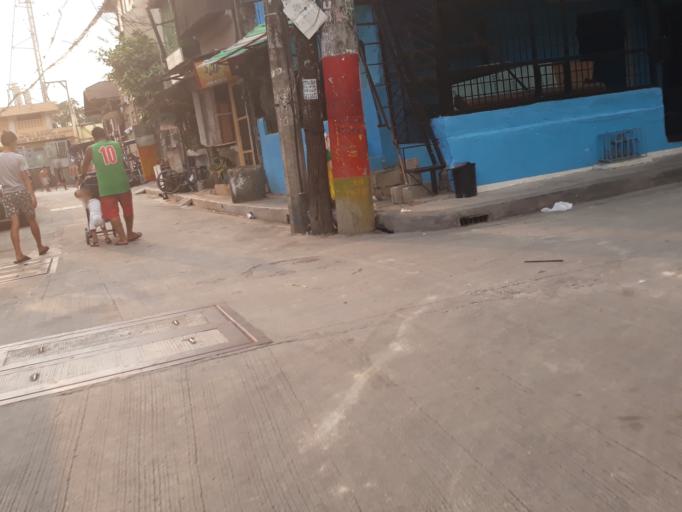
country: PH
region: Metro Manila
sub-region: San Juan
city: San Juan
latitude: 14.6096
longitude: 121.0224
